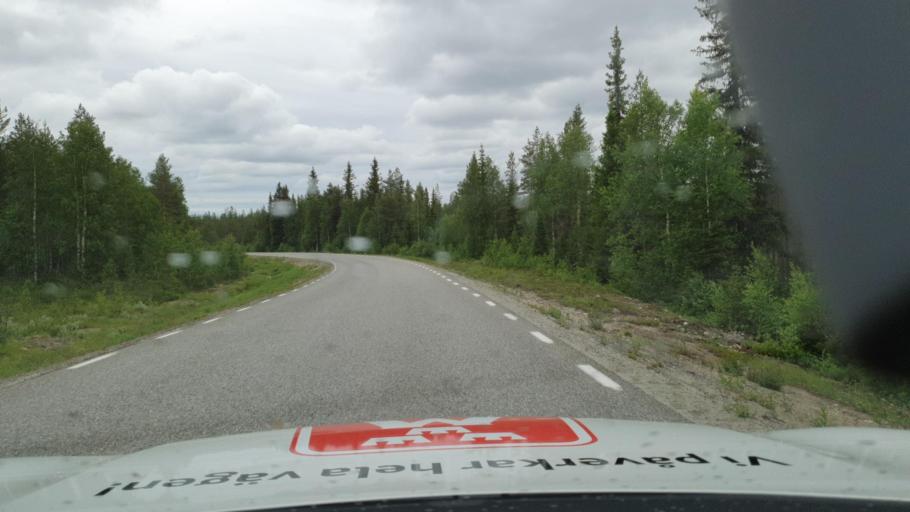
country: SE
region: Vaesterbotten
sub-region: Lycksele Kommun
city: Lycksele
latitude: 64.2270
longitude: 18.2453
